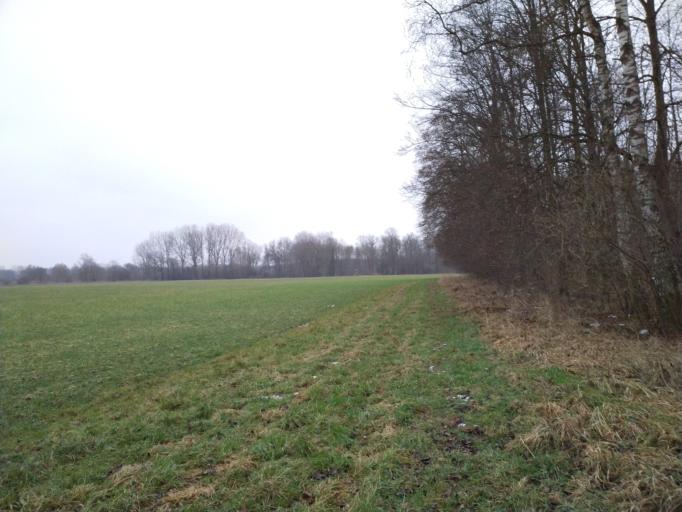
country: DE
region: Bavaria
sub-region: Swabia
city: Offingen
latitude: 48.4921
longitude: 10.3407
